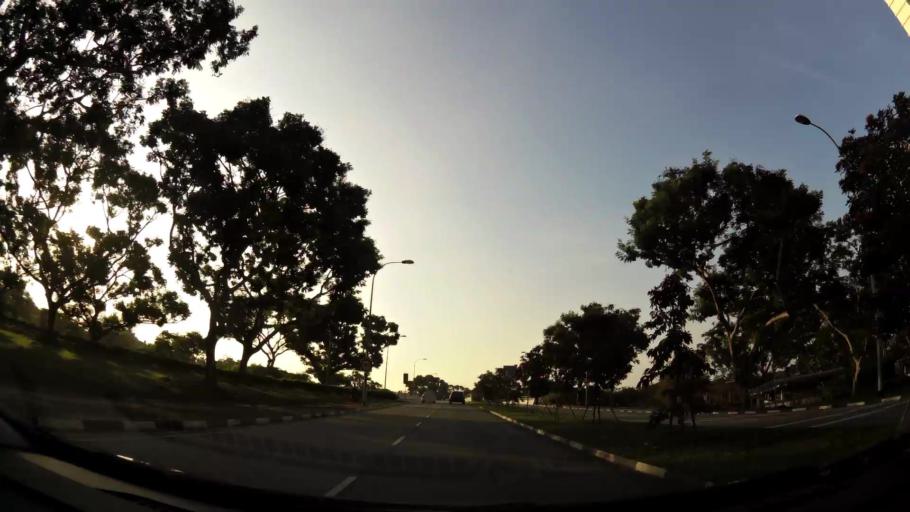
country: SG
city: Singapore
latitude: 1.3101
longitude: 103.9347
